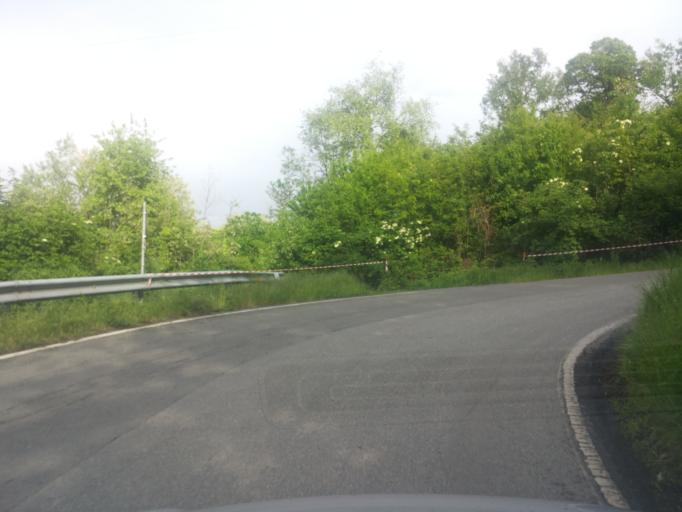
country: IT
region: Piedmont
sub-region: Provincia di Torino
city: Caravino
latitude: 45.3926
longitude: 7.9663
